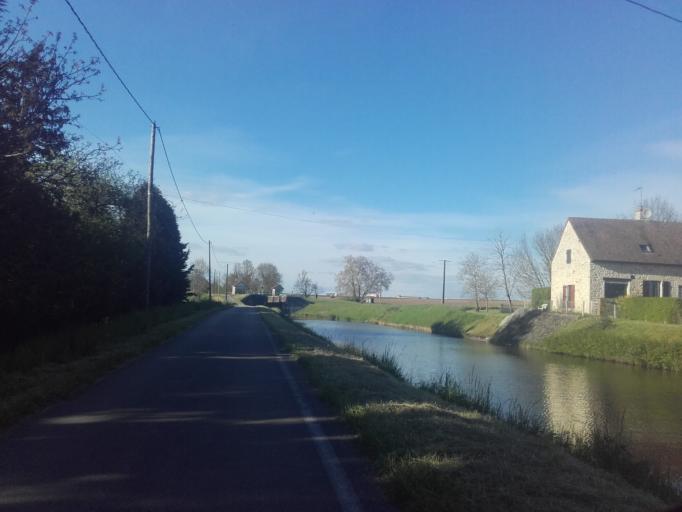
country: FR
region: Bourgogne
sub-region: Departement de Saone-et-Loire
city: Rully
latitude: 46.8836
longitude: 4.7645
